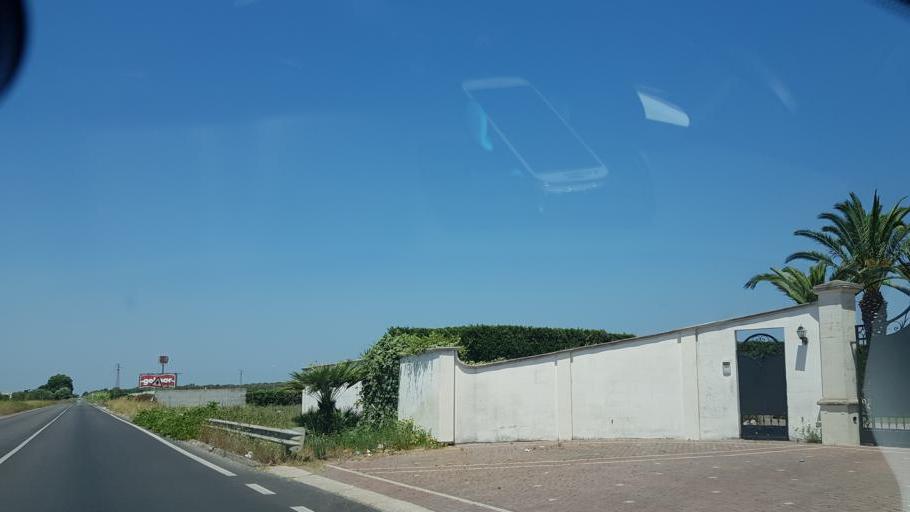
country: IT
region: Apulia
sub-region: Provincia di Lecce
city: Veglie
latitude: 40.3542
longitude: 17.9684
